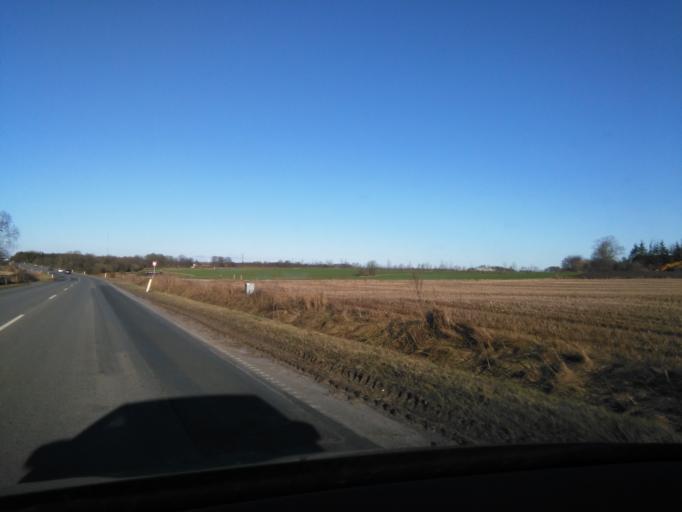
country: DK
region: North Denmark
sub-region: Mariagerfjord Kommune
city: Hobro
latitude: 56.6608
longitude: 9.8040
